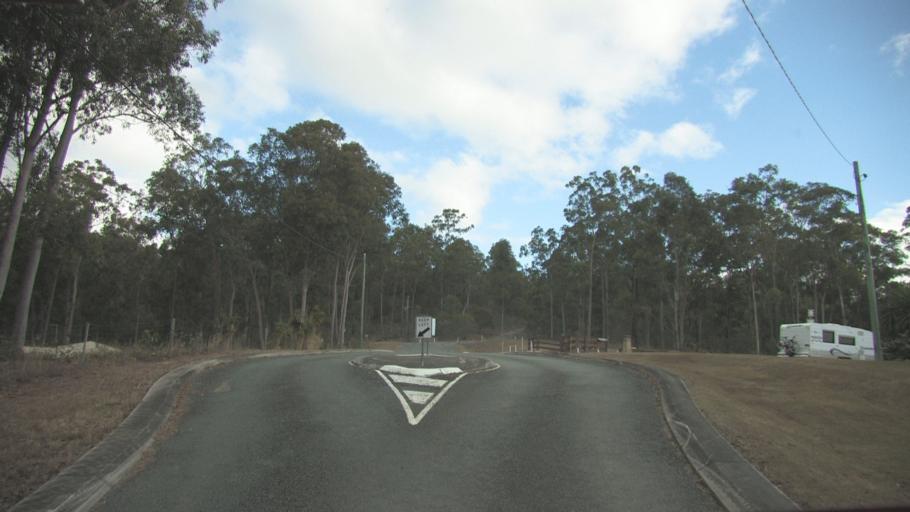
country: AU
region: Queensland
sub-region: Logan
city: Cedar Vale
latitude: -27.9337
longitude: 153.0526
